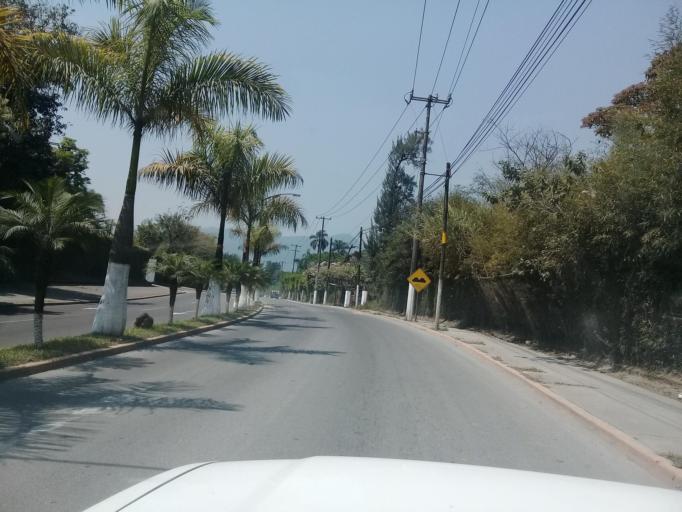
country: MX
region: Veracruz
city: Ixtac Zoquitlan
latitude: 18.8612
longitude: -97.0405
